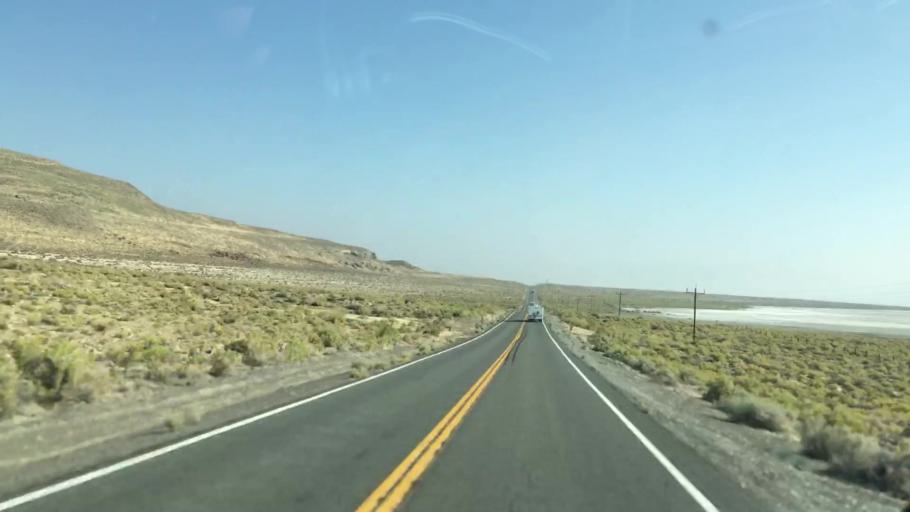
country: US
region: Nevada
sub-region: Lyon County
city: Fernley
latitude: 40.1023
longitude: -119.3705
